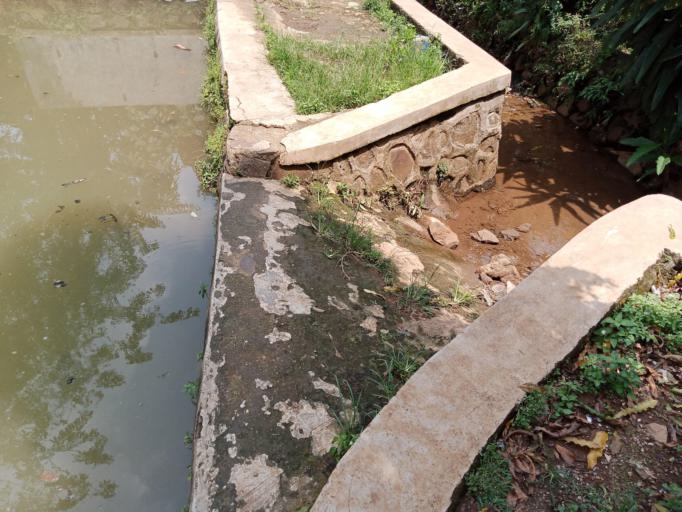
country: ID
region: West Java
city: Depok
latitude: -6.4046
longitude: 106.8097
